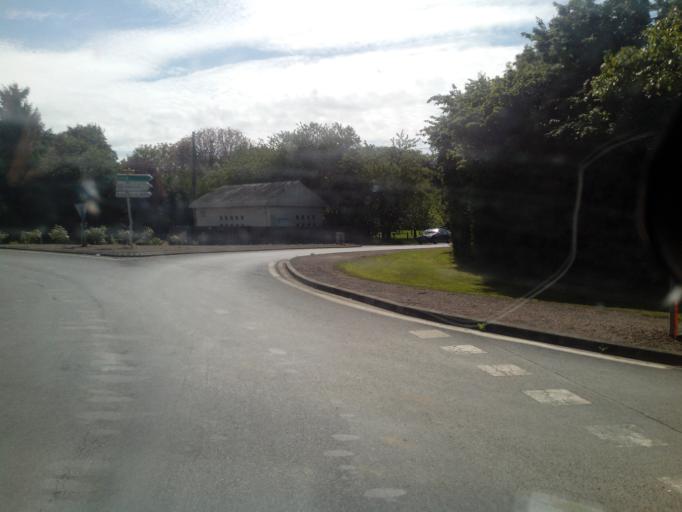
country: FR
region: Lower Normandy
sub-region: Departement du Calvados
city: Touques
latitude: 49.2605
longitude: 0.1083
